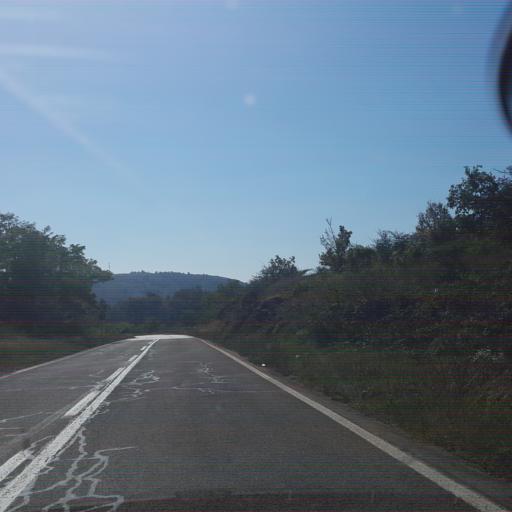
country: RS
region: Central Serbia
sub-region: Nisavski Okrug
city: Svrljig
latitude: 43.4584
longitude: 22.2056
